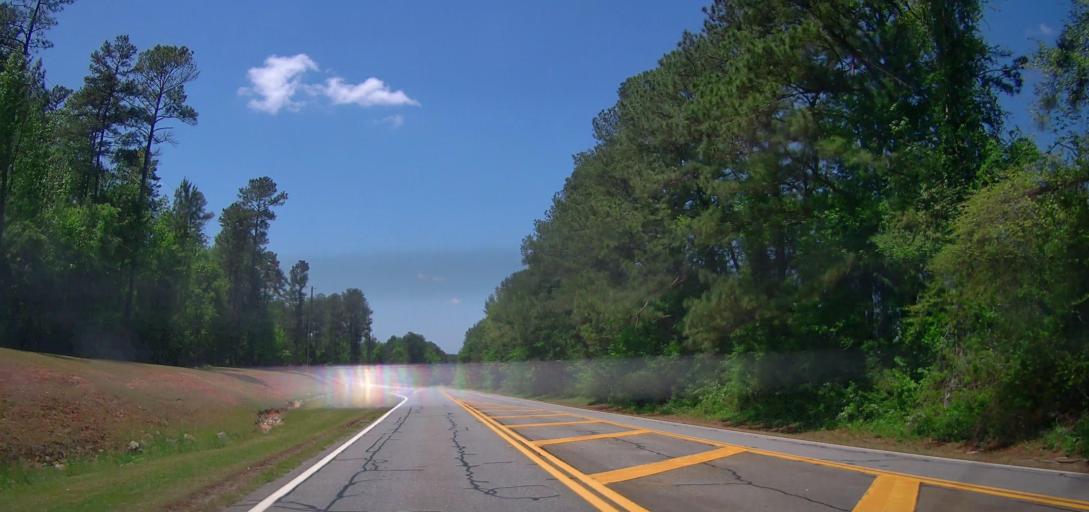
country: US
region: Georgia
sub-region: Jasper County
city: Monticello
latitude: 33.3101
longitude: -83.7038
